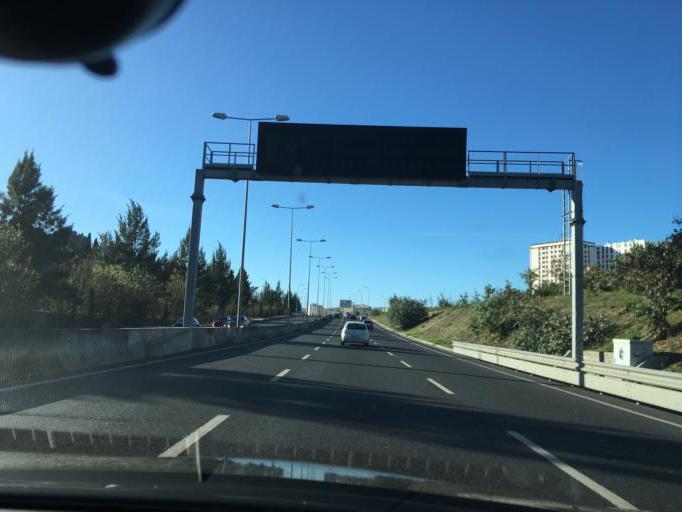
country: PT
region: Lisbon
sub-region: Odivelas
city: Pontinha
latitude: 38.7585
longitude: -9.1954
